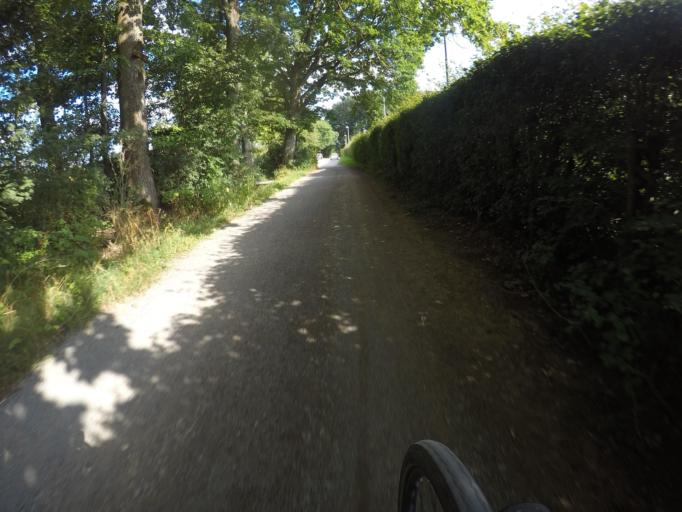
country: DE
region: Baden-Wuerttemberg
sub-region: Regierungsbezirk Stuttgart
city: Stuttgart-Ost
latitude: 48.7478
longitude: 9.2030
